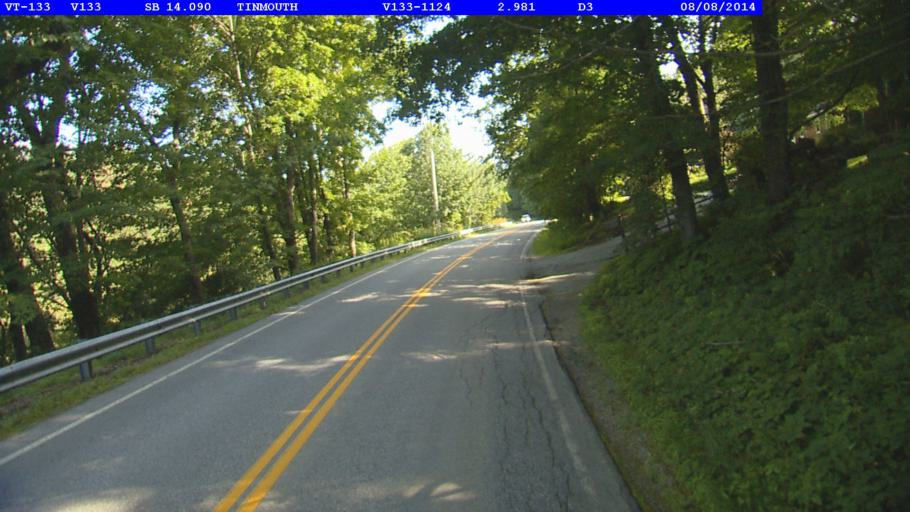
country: US
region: Vermont
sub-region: Rutland County
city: West Rutland
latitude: 43.4891
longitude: -73.0758
